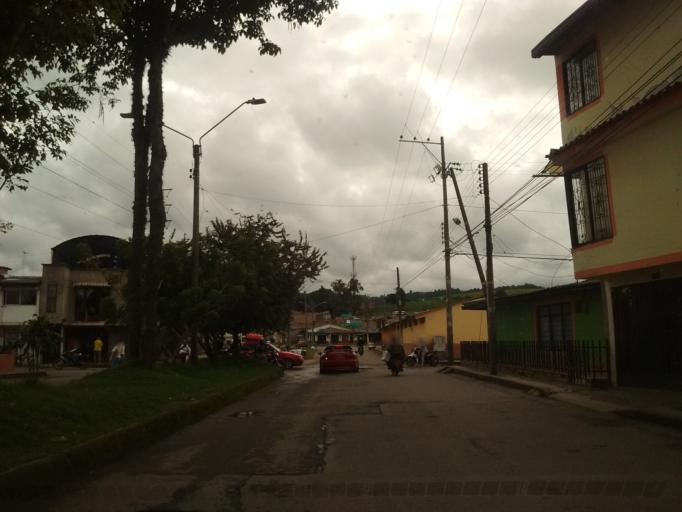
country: CO
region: Cauca
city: Popayan
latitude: 2.4327
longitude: -76.6104
